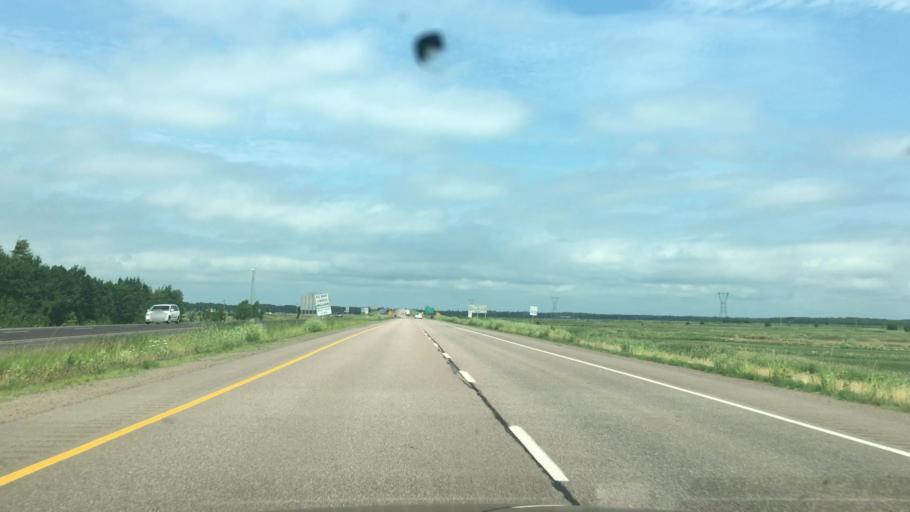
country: CA
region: Nova Scotia
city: Amherst
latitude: 45.8301
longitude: -64.2379
